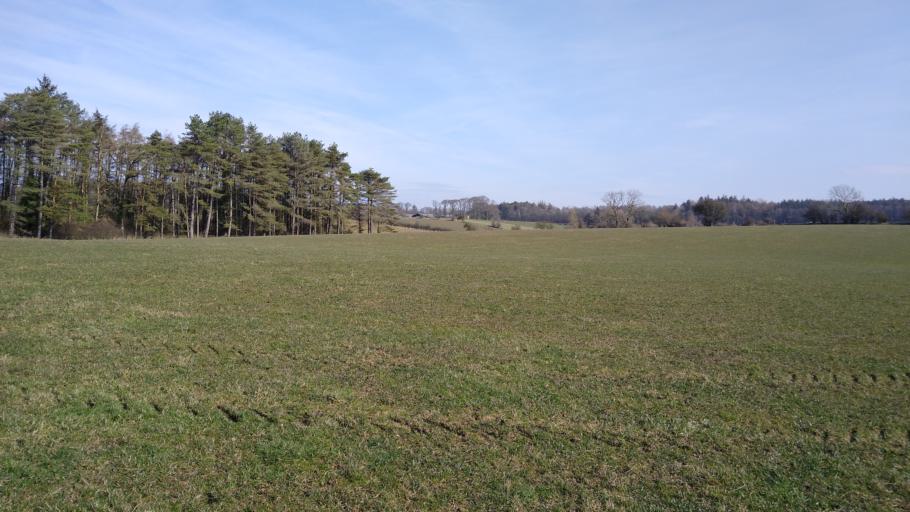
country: GB
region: England
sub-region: Cumbria
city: Cockermouth
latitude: 54.6769
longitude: -3.3969
